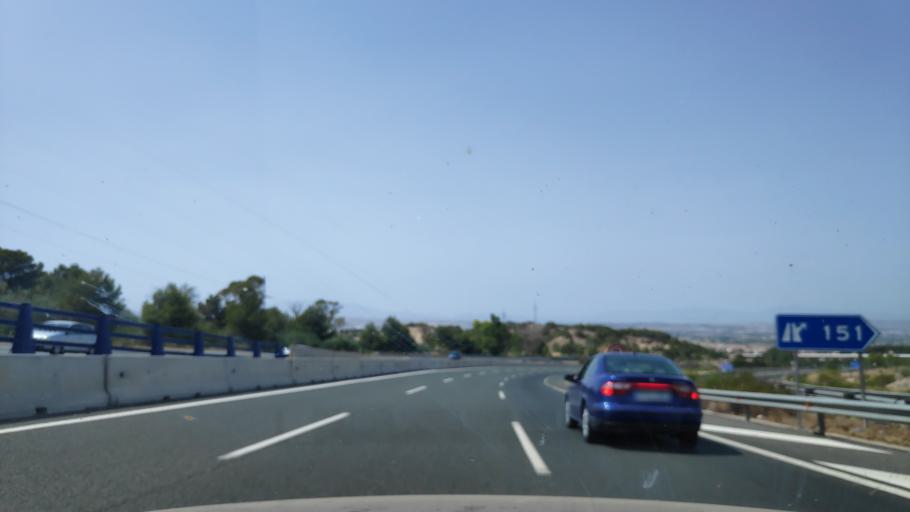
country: ES
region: Murcia
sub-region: Murcia
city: Alcantarilla
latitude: 37.9124
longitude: -1.1643
